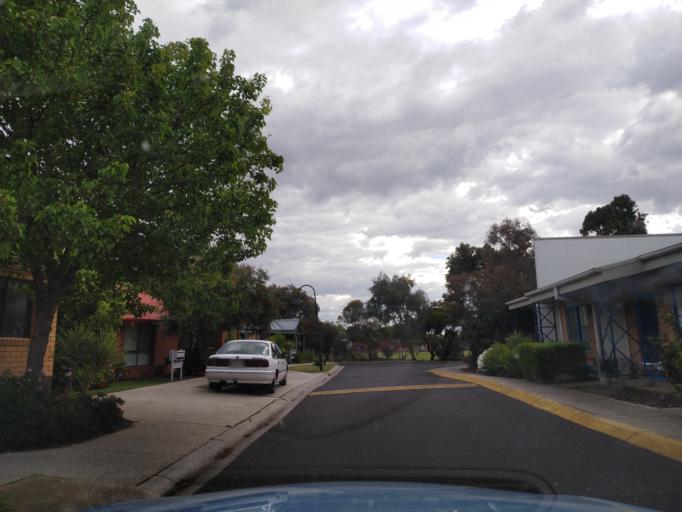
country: AU
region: Victoria
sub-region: Hobsons Bay
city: Williamstown North
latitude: -37.8549
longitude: 144.8787
